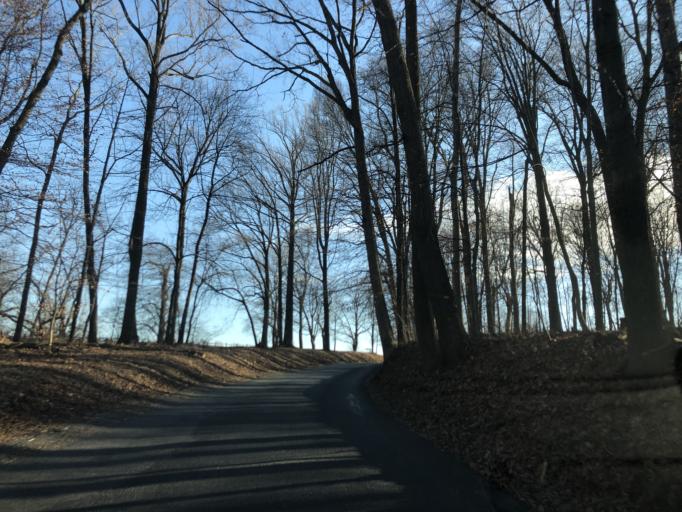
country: US
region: Pennsylvania
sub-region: Chester County
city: Upland
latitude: 39.8904
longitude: -75.7754
